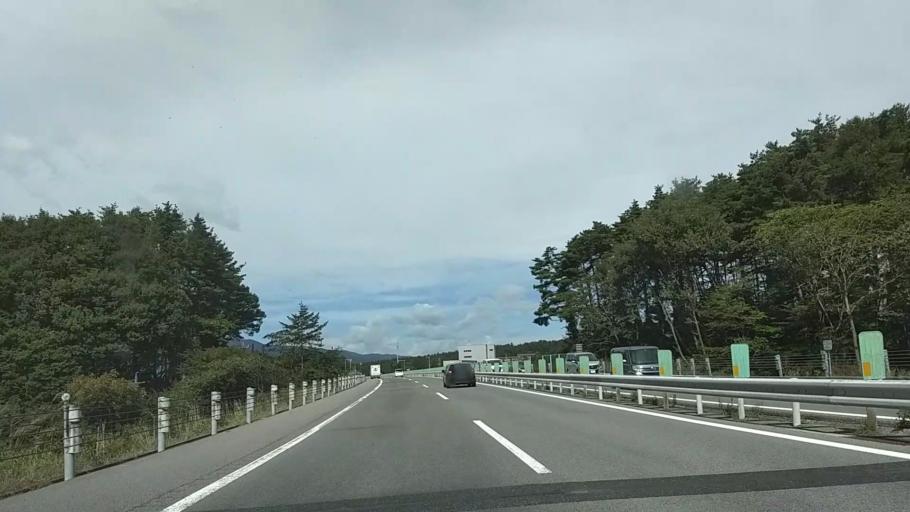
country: JP
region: Nagano
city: Chino
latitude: 35.8947
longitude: 138.2816
